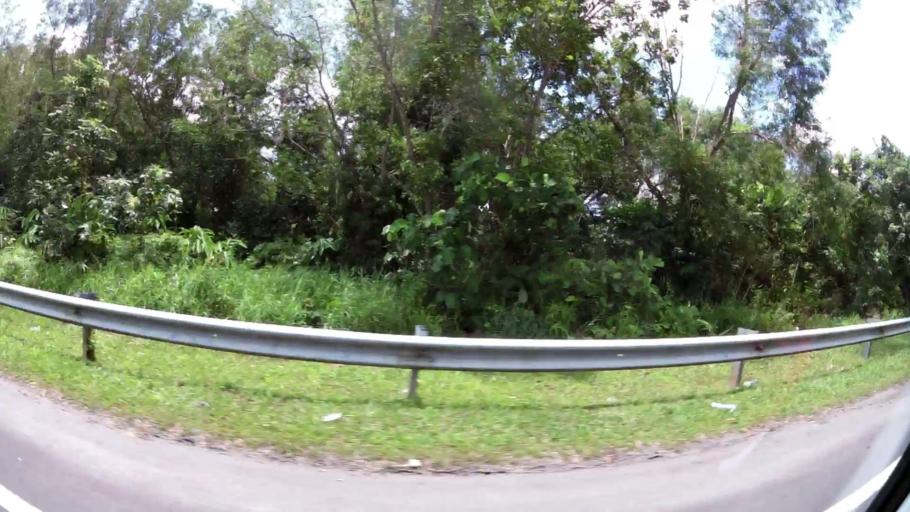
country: BN
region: Brunei and Muara
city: Bandar Seri Begawan
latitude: 4.9266
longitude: 114.9616
